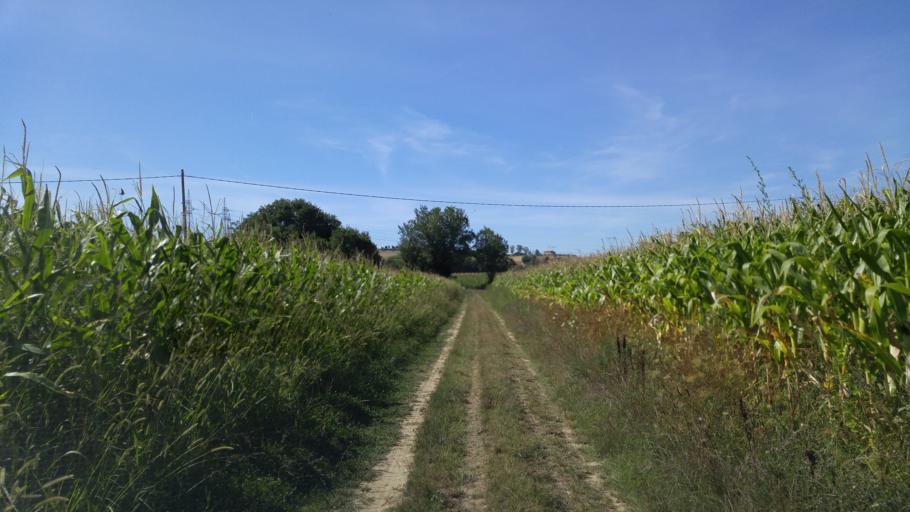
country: IT
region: The Marches
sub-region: Provincia di Pesaro e Urbino
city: Cuccurano
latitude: 43.7839
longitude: 12.9556
